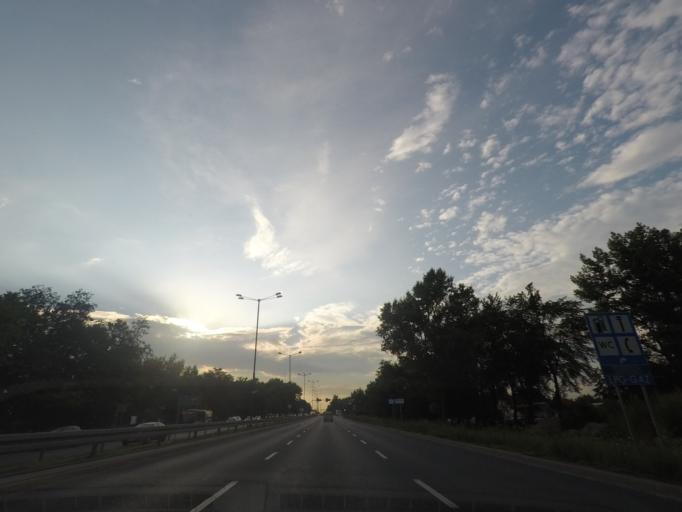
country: PL
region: Lesser Poland Voivodeship
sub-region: Powiat wielicki
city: Czarnochowice
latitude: 50.0095
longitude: 20.0105
